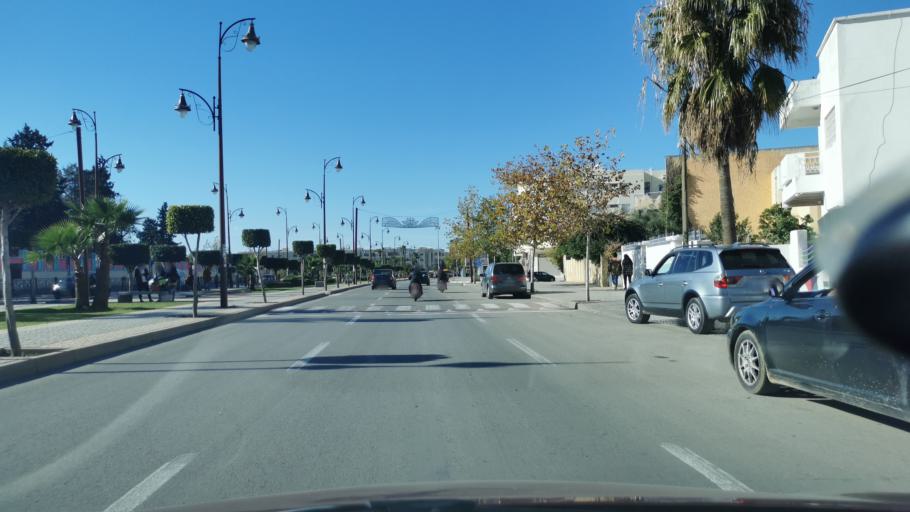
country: MA
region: Fes-Boulemane
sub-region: Fes
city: Fes
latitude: 34.0164
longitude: -5.0163
